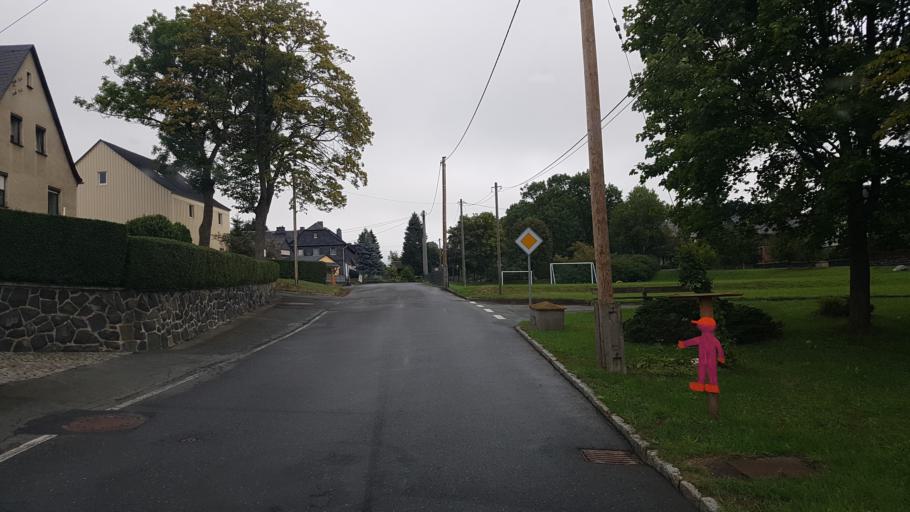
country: DE
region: Thuringia
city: Bad Lobenstein
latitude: 50.4871
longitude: 11.6059
